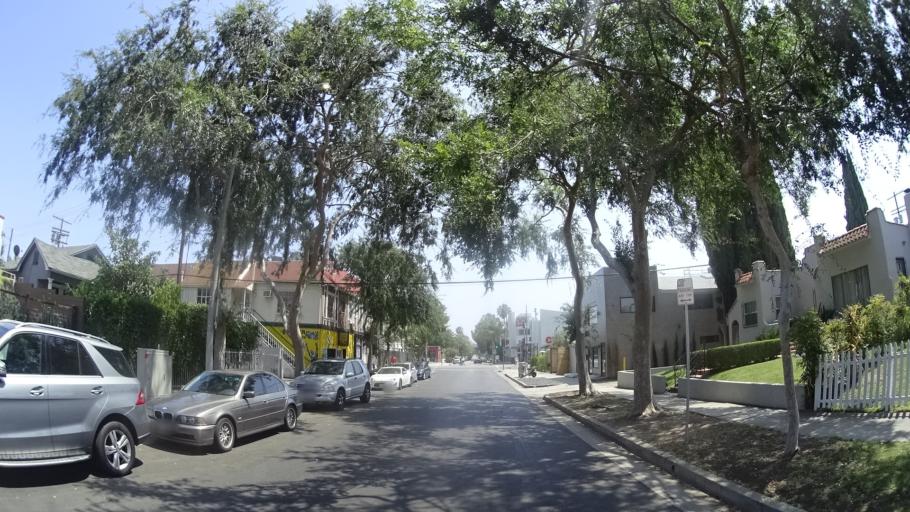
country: US
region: California
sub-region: Los Angeles County
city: West Hollywood
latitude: 34.0844
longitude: -118.3532
